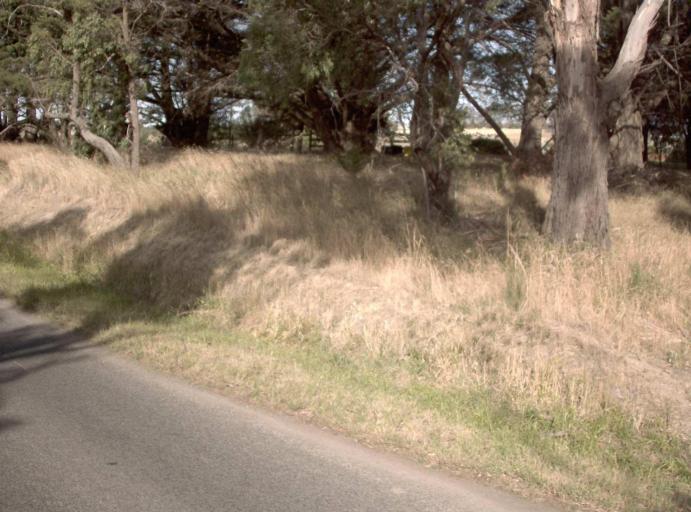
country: AU
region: Victoria
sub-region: Latrobe
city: Morwell
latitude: -38.2745
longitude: 146.4667
